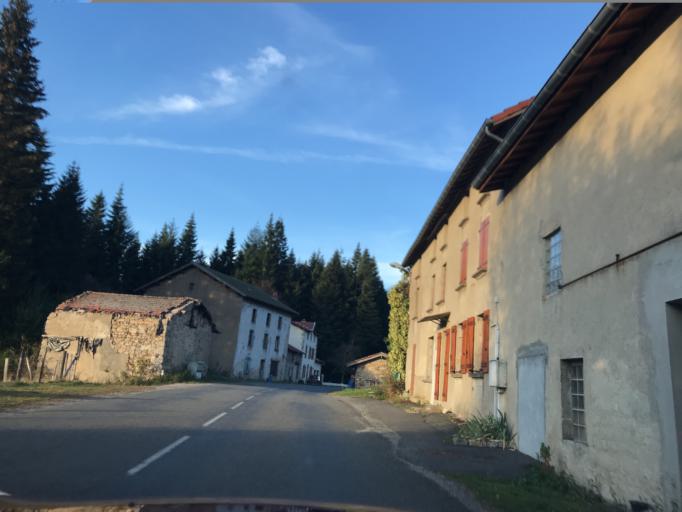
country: FR
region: Rhone-Alpes
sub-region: Departement de la Loire
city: Noiretable
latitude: 45.8019
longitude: 3.7147
